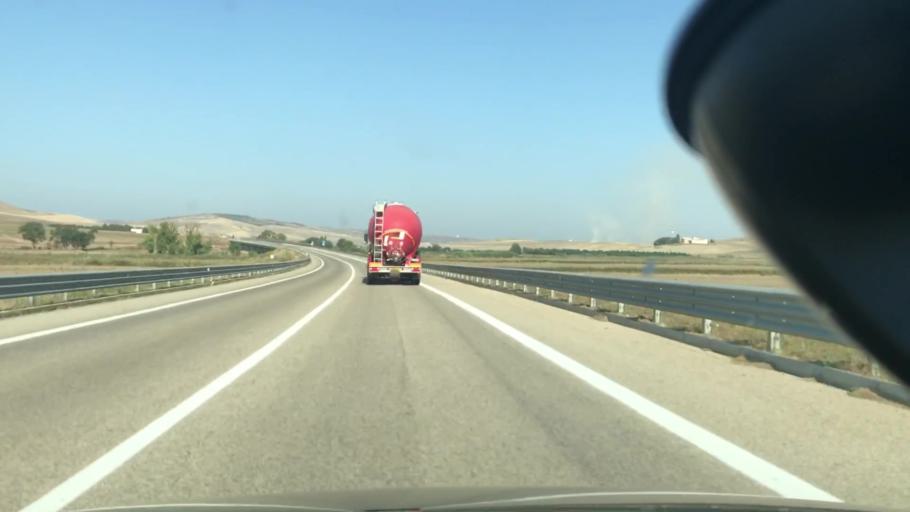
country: IT
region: Basilicate
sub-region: Provincia di Matera
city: Irsina
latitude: 40.7806
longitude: 16.3143
